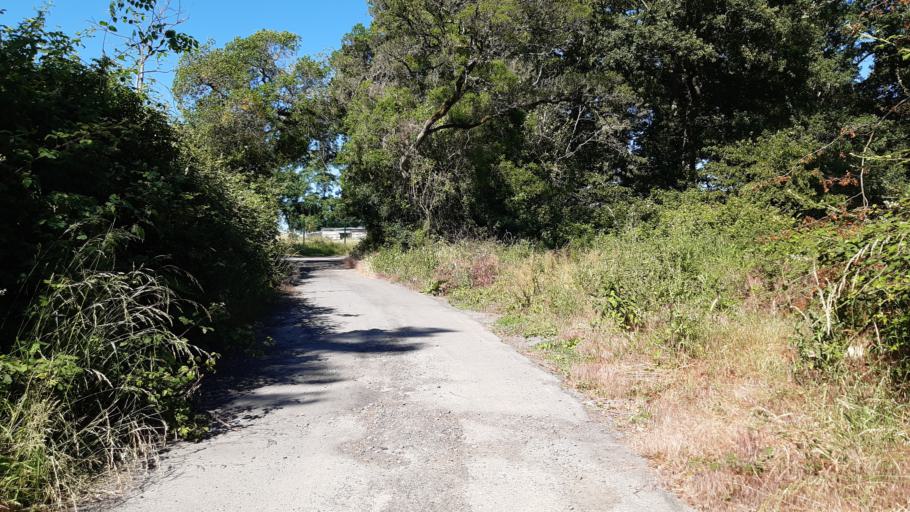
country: FR
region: Centre
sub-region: Departement d'Indre-et-Loire
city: Mettray
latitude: 47.4344
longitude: 0.6590
